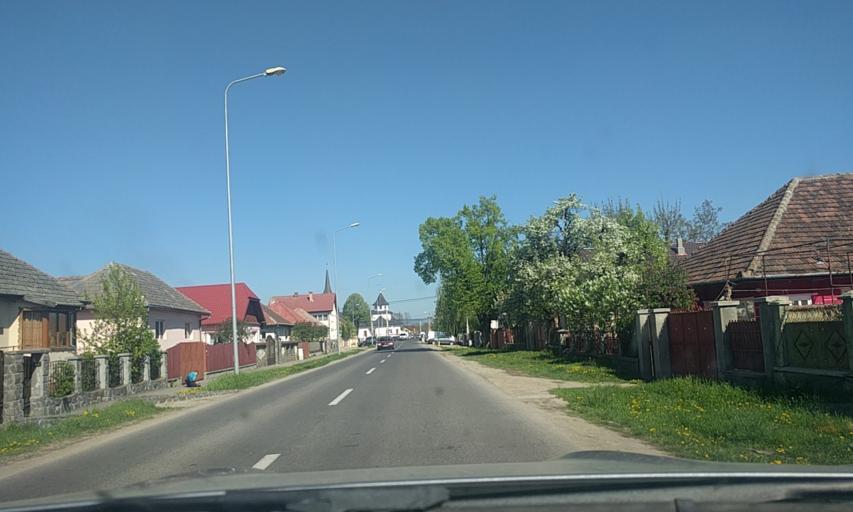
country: RO
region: Brasov
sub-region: Comuna Ghimbav
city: Ghimbav
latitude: 45.6968
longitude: 25.5595
